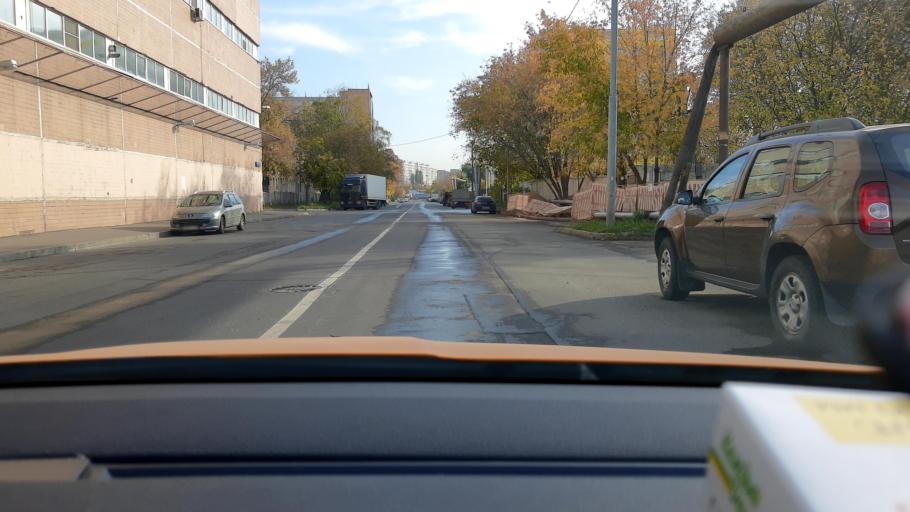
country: RU
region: Moscow
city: Slobodka
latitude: 55.8698
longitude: 37.5753
